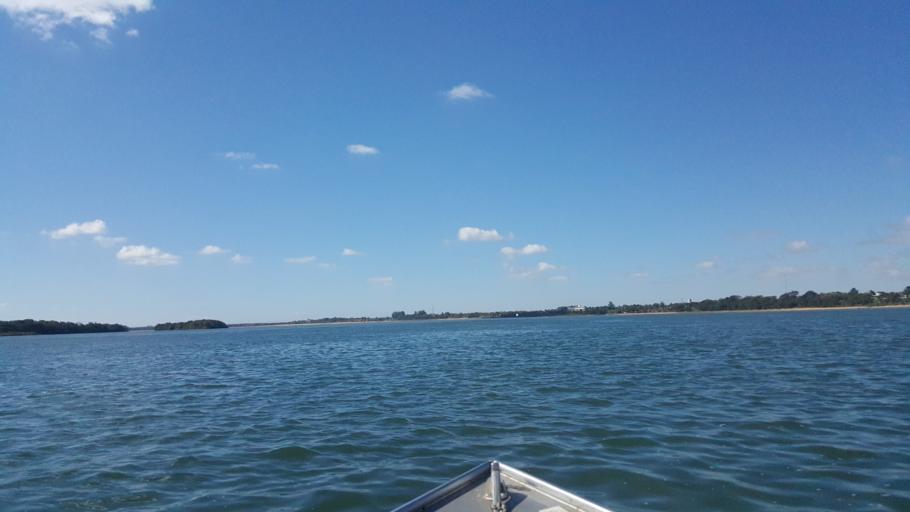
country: AR
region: Corrientes
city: Ituzaingo
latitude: -27.5815
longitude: -56.7010
